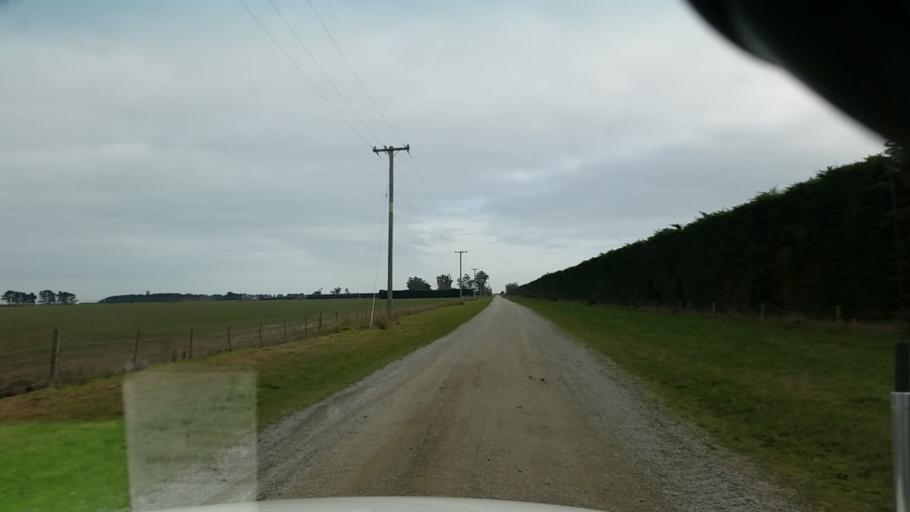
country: NZ
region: Canterbury
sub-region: Ashburton District
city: Tinwald
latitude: -44.0608
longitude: 171.7662
